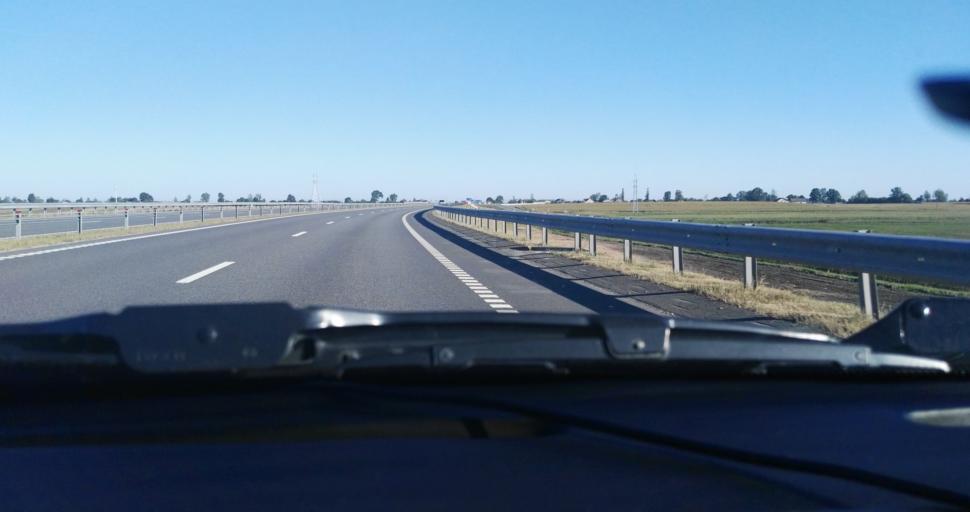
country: BY
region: Gomel
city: Buda-Kashalyova
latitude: 52.5110
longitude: 30.6309
